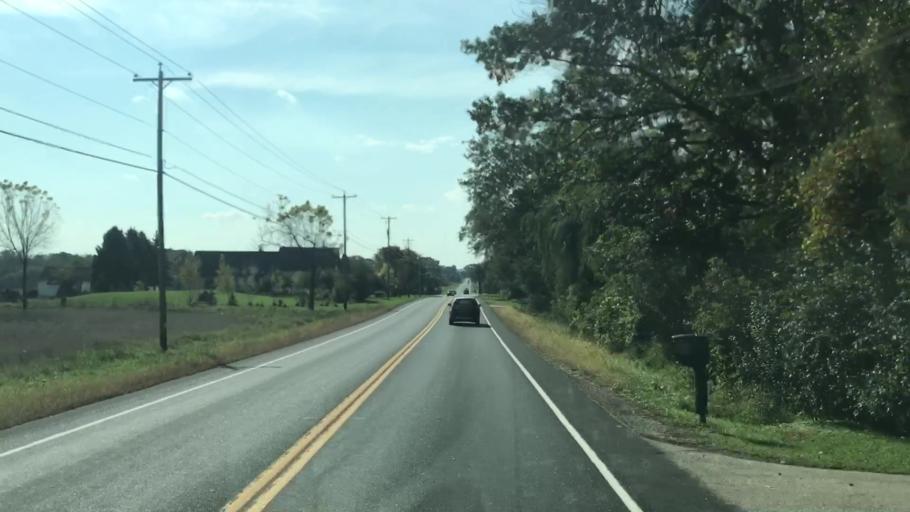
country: US
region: Wisconsin
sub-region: Ozaukee County
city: Mequon
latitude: 43.2093
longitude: -88.0435
